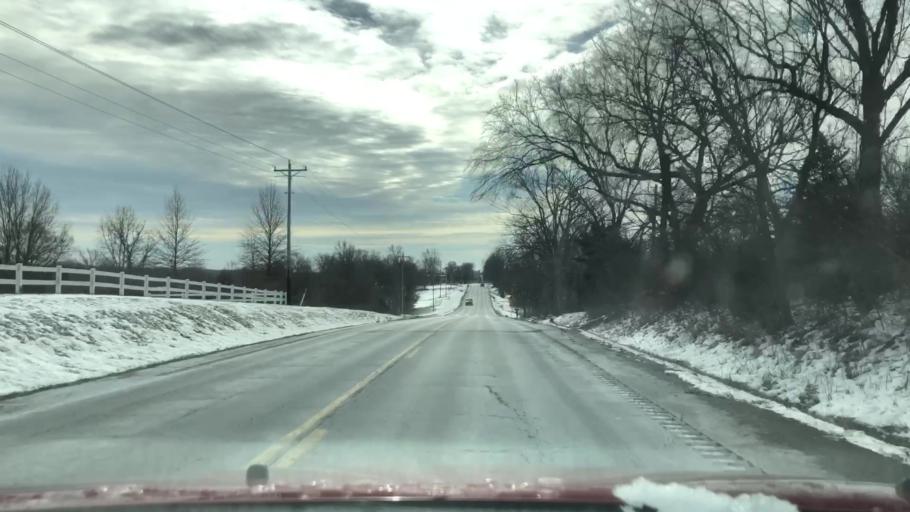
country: US
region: Missouri
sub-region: Jackson County
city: Lone Jack
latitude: 38.8774
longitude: -94.1352
